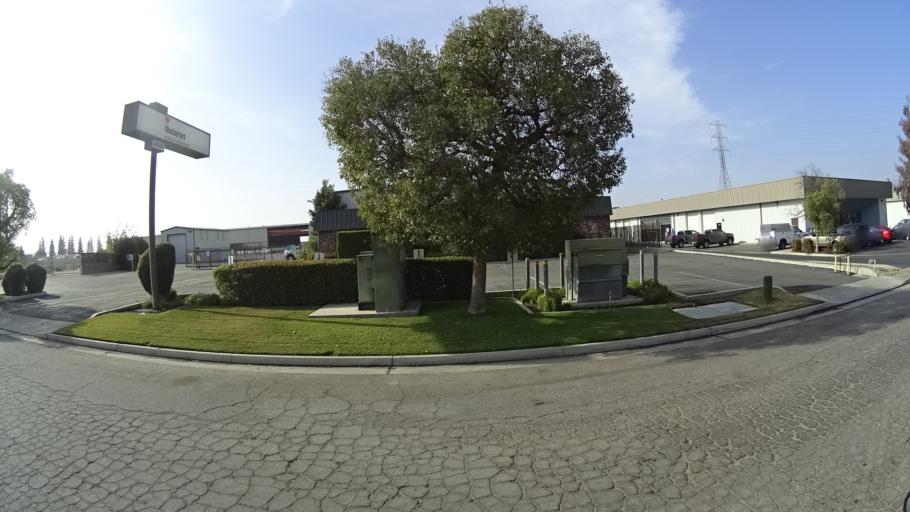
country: US
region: California
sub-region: Kern County
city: Greenacres
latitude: 35.3963
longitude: -119.0800
